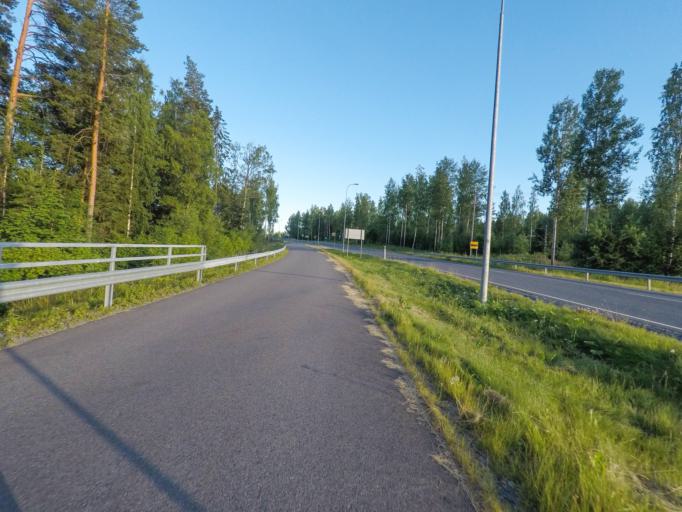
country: FI
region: Northern Savo
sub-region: Kuopio
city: Kuopio
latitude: 62.9370
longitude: 27.6679
